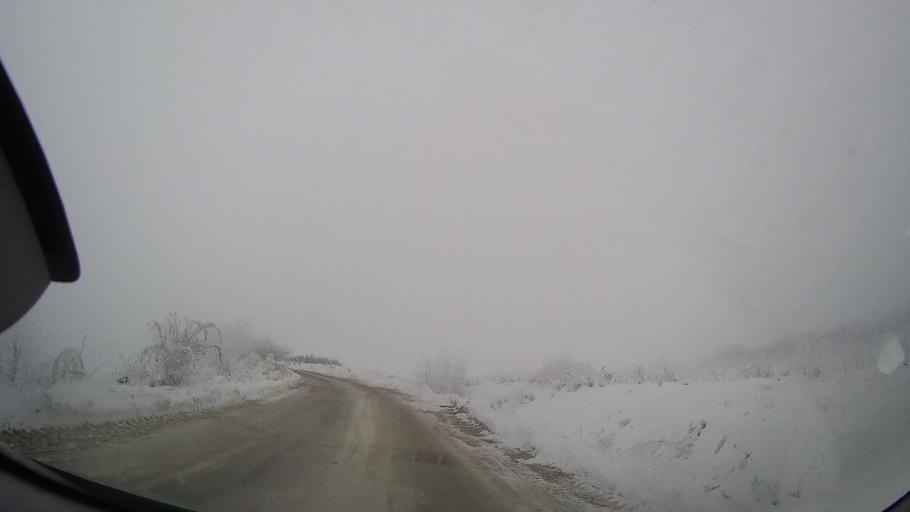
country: RO
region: Iasi
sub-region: Comuna Dagata
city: Dagata
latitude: 46.9232
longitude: 27.1736
